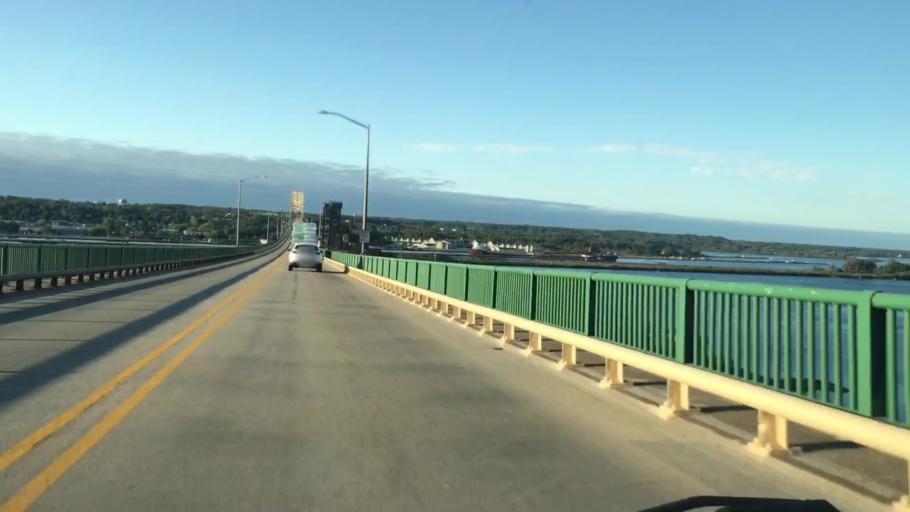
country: US
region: Michigan
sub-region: Chippewa County
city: Sault Ste. Marie
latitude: 46.5117
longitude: -84.3595
